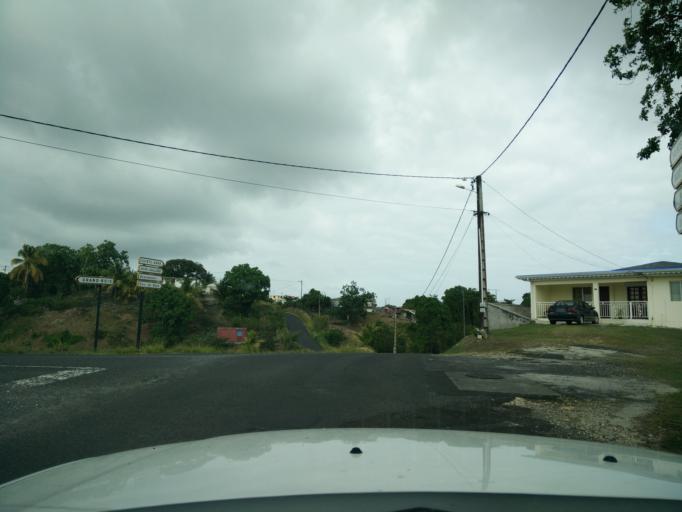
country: GP
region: Guadeloupe
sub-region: Guadeloupe
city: Le Gosier
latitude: 16.2402
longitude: -61.4481
